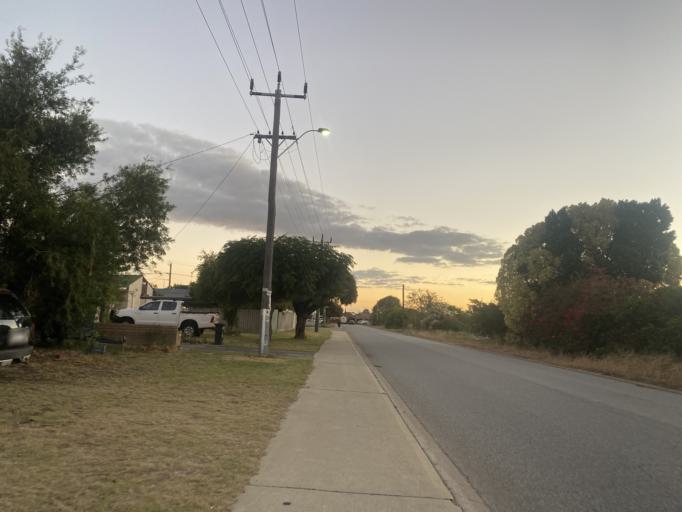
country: AU
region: Western Australia
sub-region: Belmont
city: Kewdale
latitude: -31.9860
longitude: 115.9932
